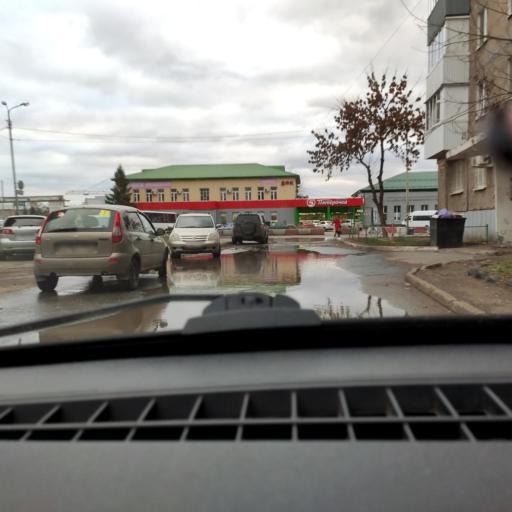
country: RU
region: Bashkortostan
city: Ufa
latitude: 54.7749
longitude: 56.1252
